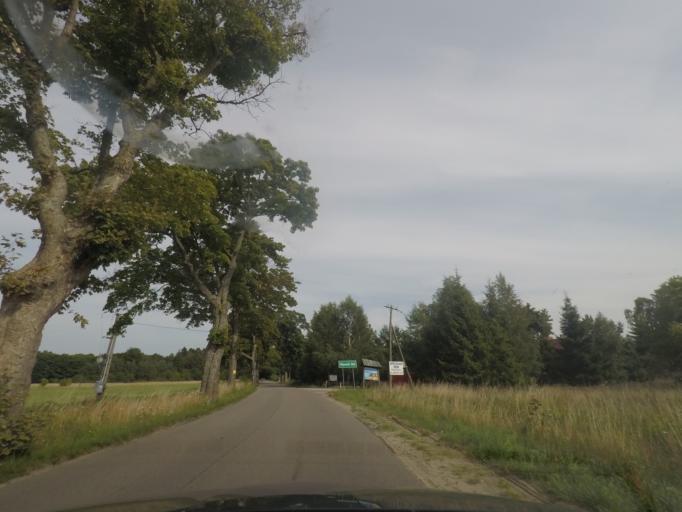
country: PL
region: Pomeranian Voivodeship
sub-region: Slupsk
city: Slupsk
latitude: 54.5958
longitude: 17.0651
